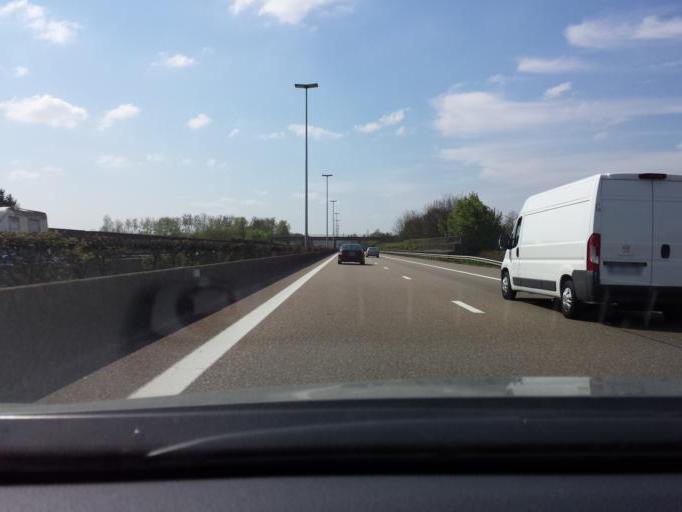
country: BE
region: Flanders
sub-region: Provincie Vlaams-Brabant
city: Holsbeek
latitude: 50.9483
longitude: 4.7815
